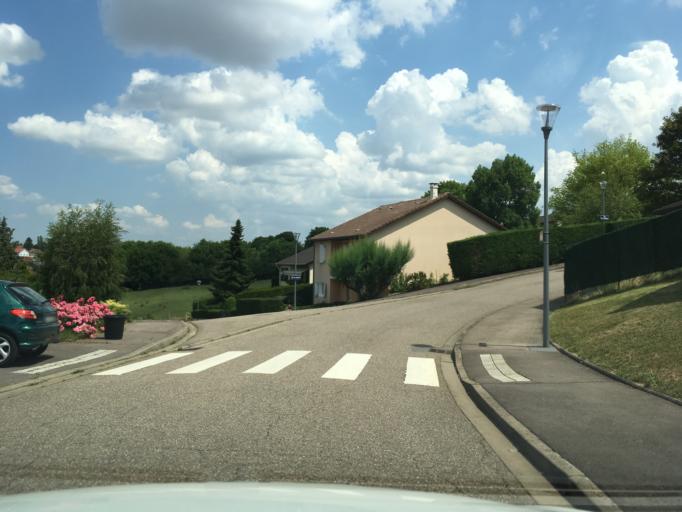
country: FR
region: Lorraine
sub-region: Departement de la Moselle
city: Saint-Julien-les-Metz
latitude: 49.1266
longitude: 6.2268
